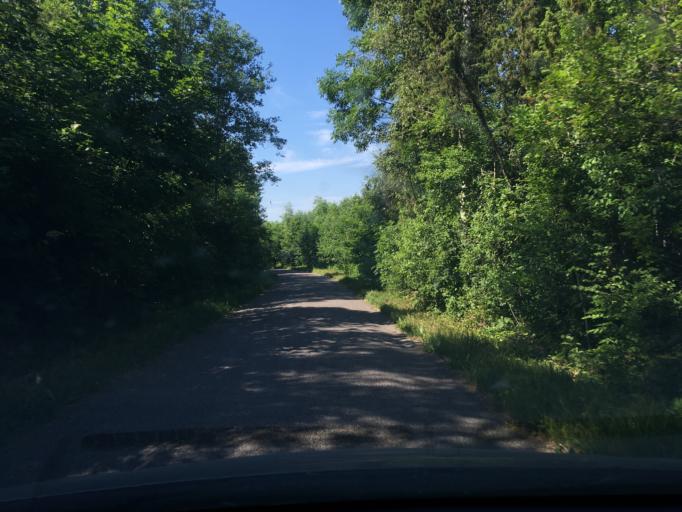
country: EE
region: Laeaene
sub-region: Lihula vald
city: Lihula
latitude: 58.5801
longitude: 23.5972
